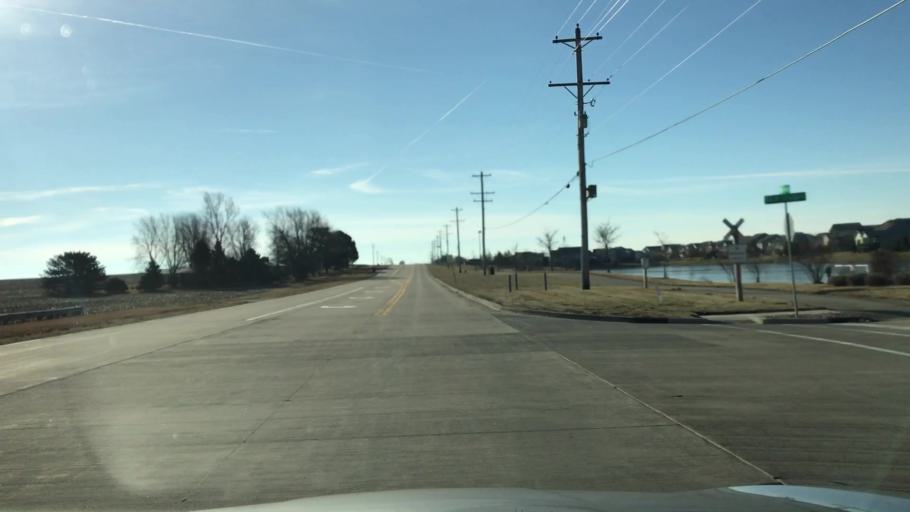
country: US
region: Illinois
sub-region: McLean County
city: Normal
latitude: 40.5572
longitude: -88.9446
